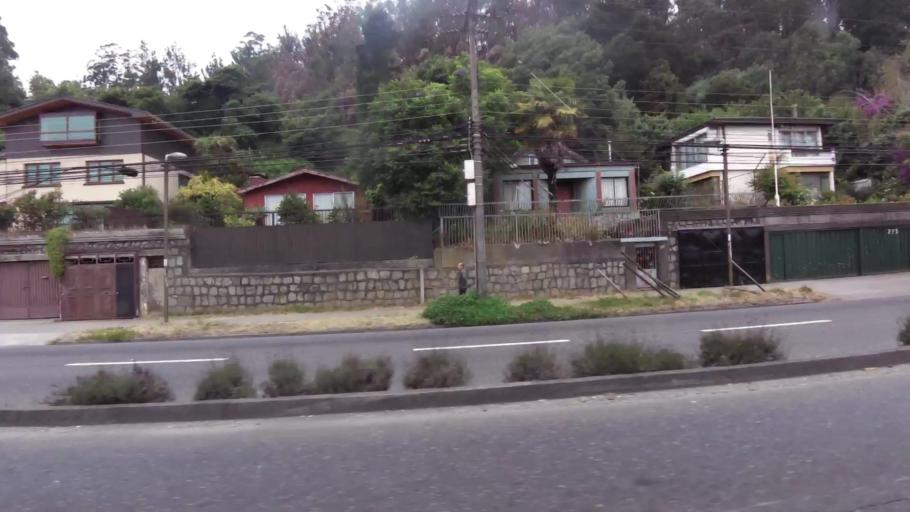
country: CL
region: Biobio
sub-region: Provincia de Concepcion
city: Concepcion
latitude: -36.8378
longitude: -73.0557
